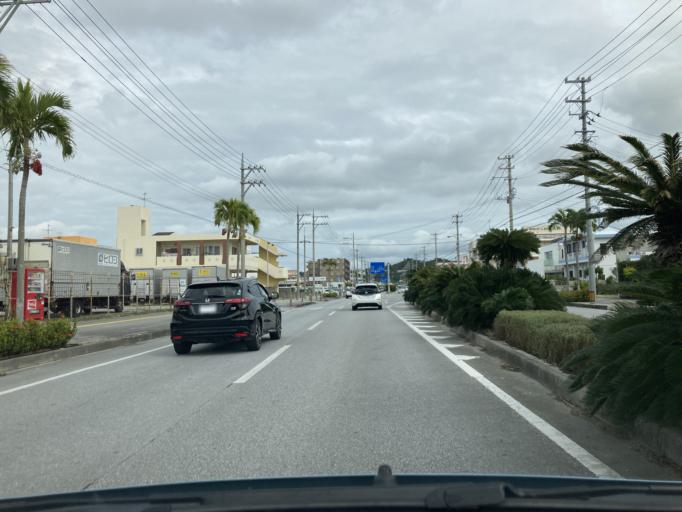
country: JP
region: Okinawa
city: Tomigusuku
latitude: 26.1613
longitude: 127.6652
